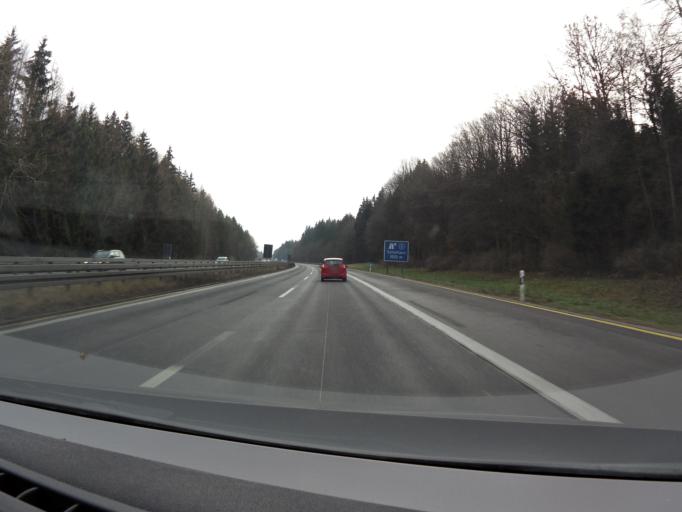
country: DE
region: Bavaria
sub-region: Upper Bavaria
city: Schaftlarn
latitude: 48.0079
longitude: 11.4190
